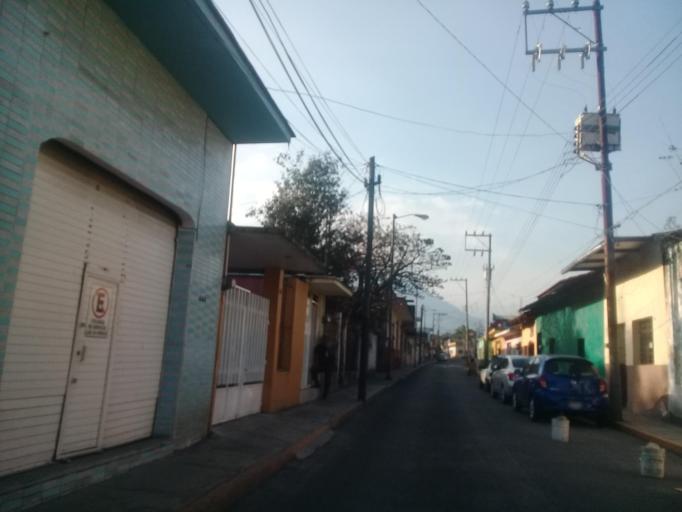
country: MX
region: Veracruz
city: Orizaba
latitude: 18.8534
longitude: -97.1092
